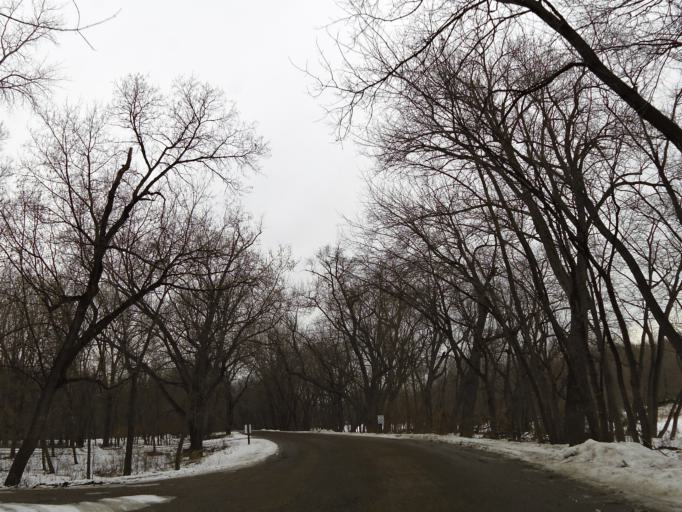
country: US
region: Minnesota
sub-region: Dakota County
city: Mendota Heights
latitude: 44.8819
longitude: -93.1797
